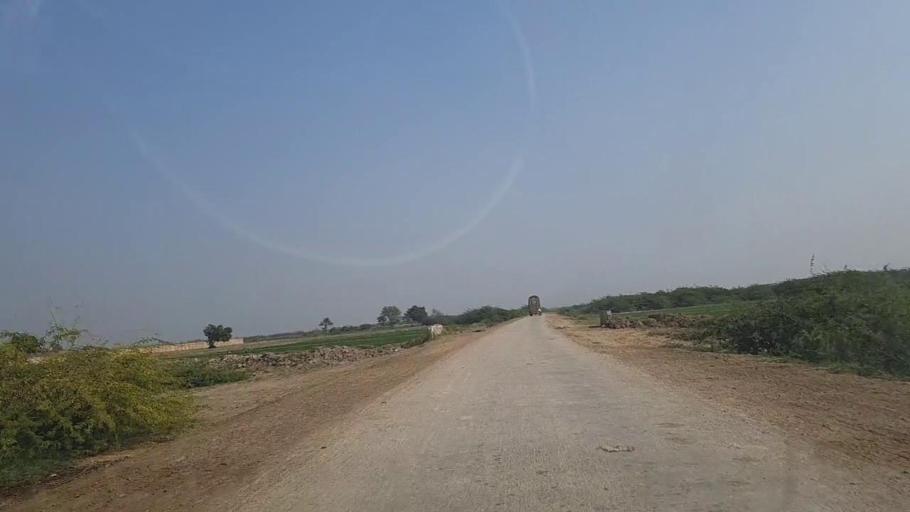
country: PK
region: Sindh
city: Keti Bandar
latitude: 24.2435
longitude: 67.7049
